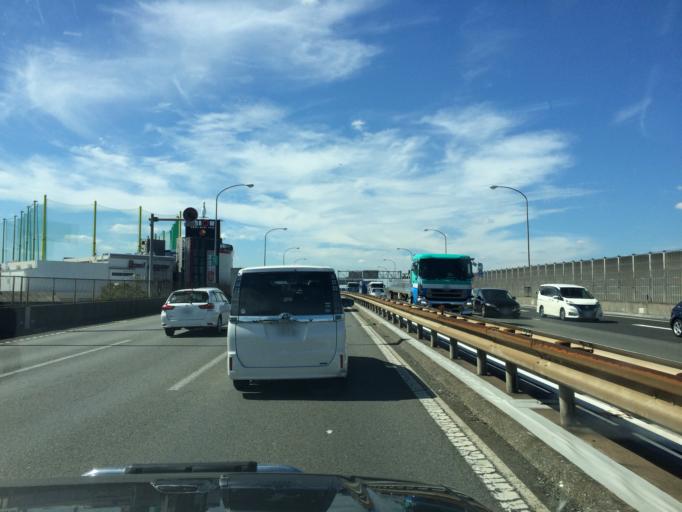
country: JP
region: Osaka
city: Matsubara
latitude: 34.5869
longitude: 135.5729
